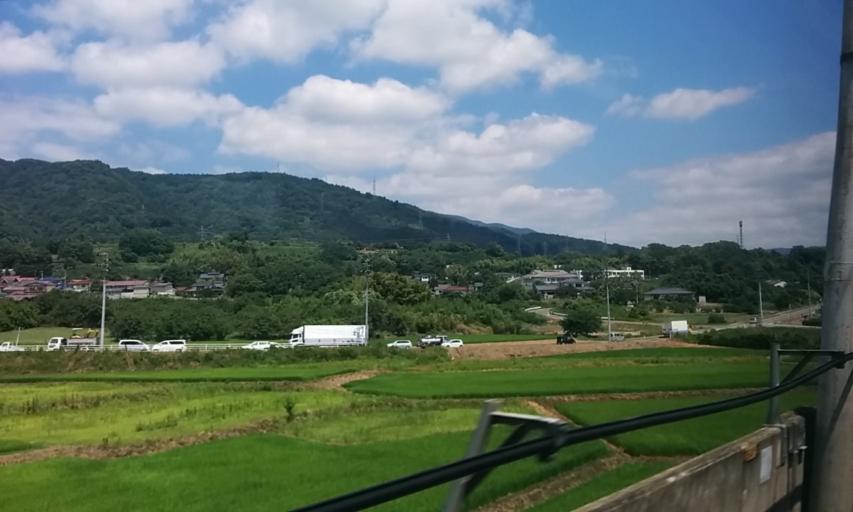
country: JP
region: Fukushima
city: Hobaramachi
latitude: 37.8342
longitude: 140.5007
